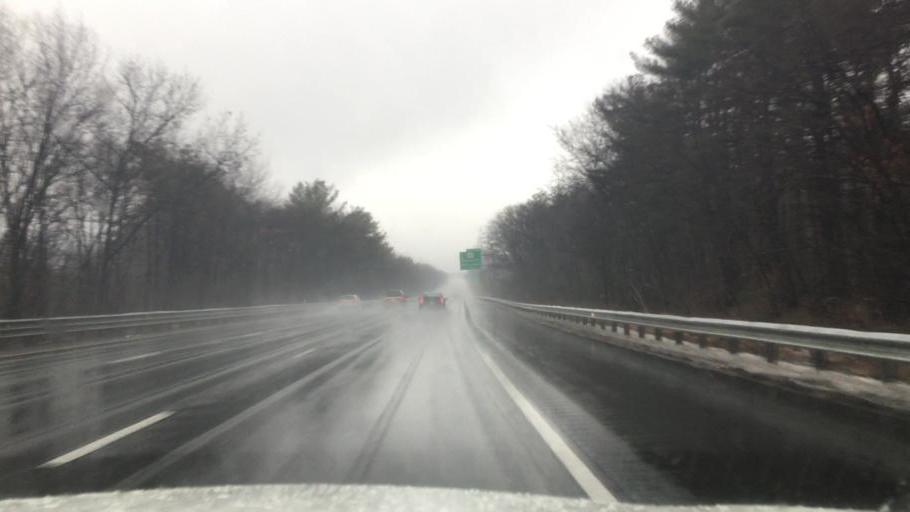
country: US
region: Massachusetts
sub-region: Essex County
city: Haverhill
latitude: 42.8056
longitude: -71.0719
